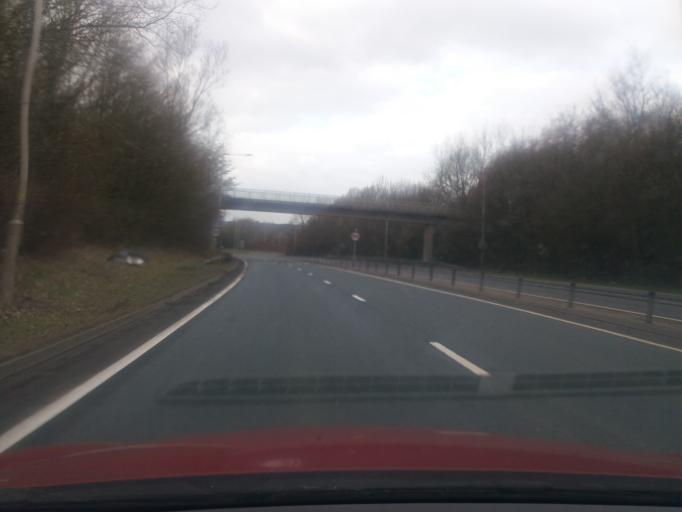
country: GB
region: England
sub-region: Lancashire
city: Leyland
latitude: 53.7412
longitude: -2.6809
